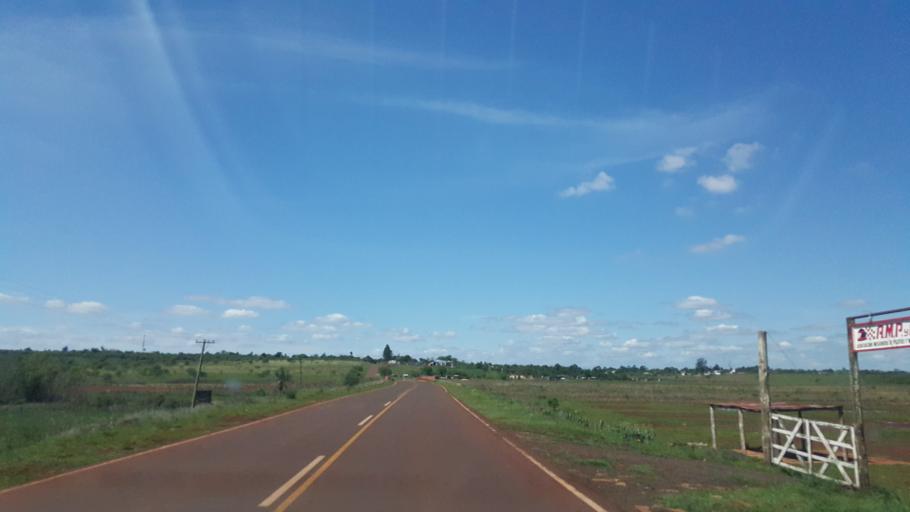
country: AR
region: Misiones
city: Garupa
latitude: -27.4942
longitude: -55.8390
